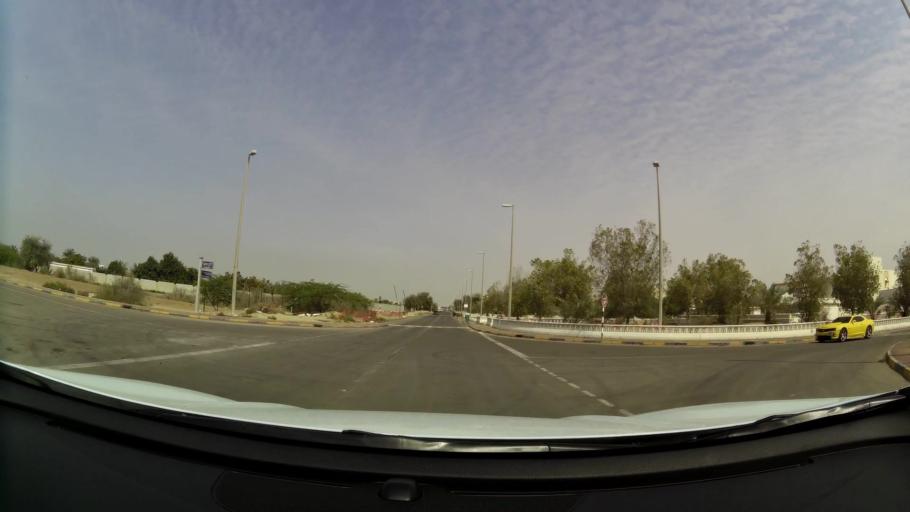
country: AE
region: Abu Dhabi
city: Abu Dhabi
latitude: 24.5294
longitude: 54.6655
